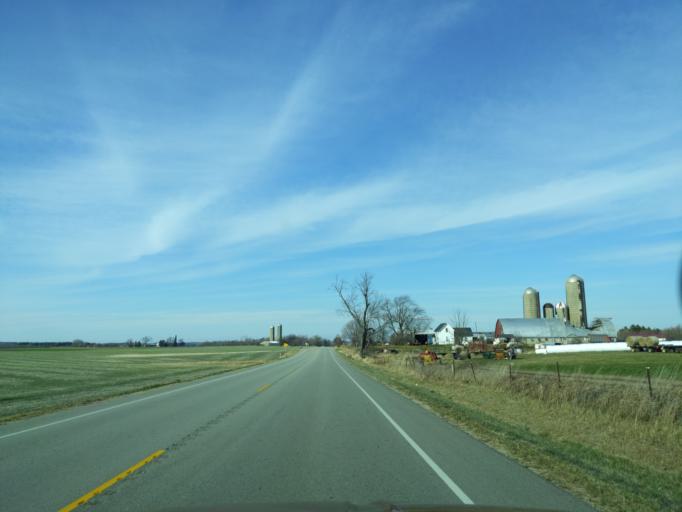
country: US
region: Wisconsin
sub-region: Walworth County
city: Elkhorn
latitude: 42.6993
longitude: -88.5706
